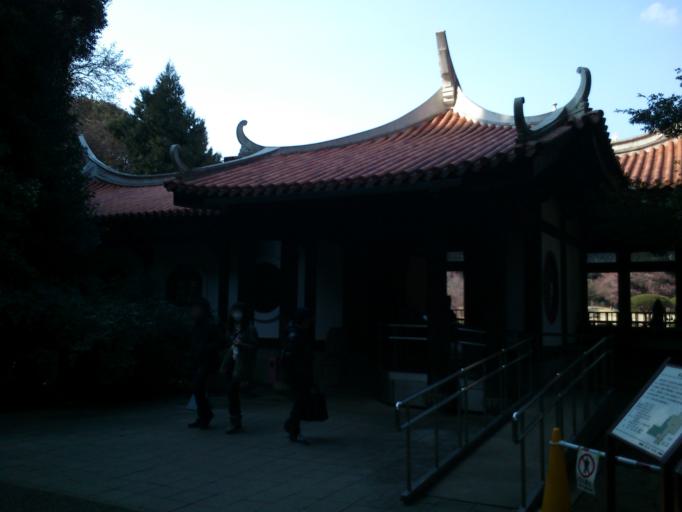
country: JP
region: Tokyo
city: Tokyo
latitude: 35.6844
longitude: 139.7087
